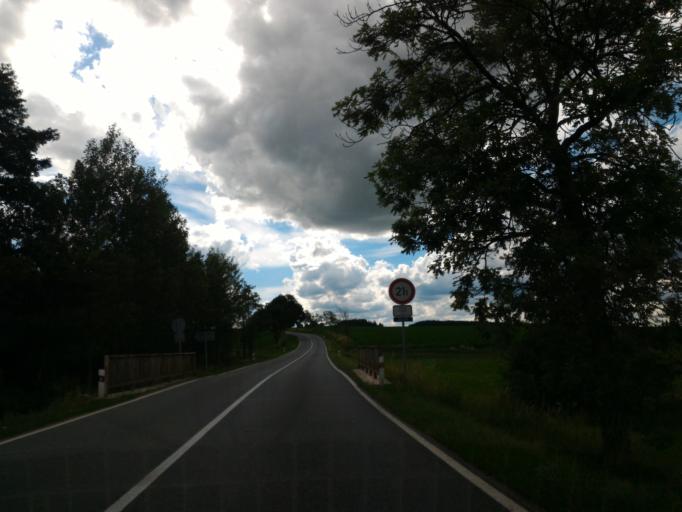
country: CZ
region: Vysocina
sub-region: Okres Jihlava
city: Polna
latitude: 49.4432
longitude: 15.7604
